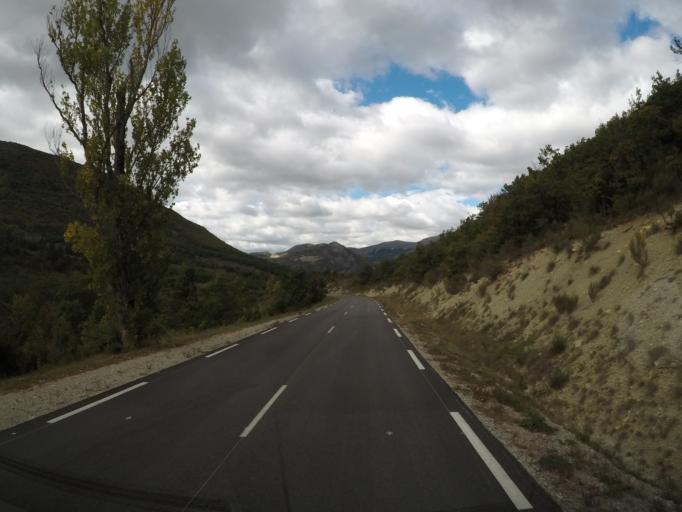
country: FR
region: Provence-Alpes-Cote d'Azur
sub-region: Departement du Vaucluse
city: Sault
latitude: 44.1815
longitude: 5.5637
